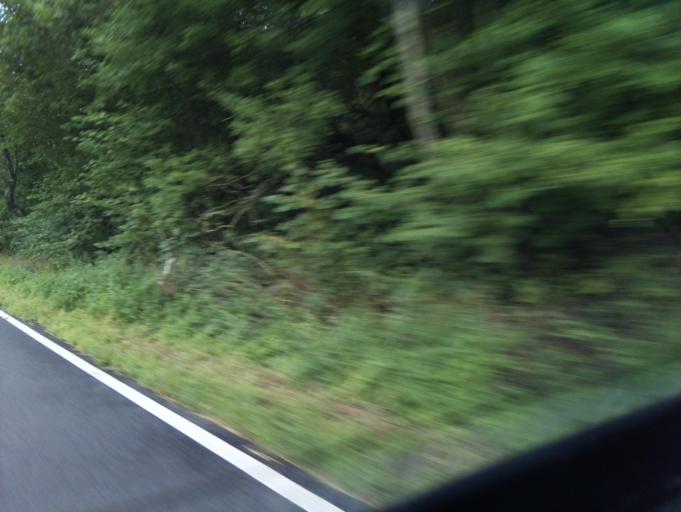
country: GB
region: England
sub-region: North Yorkshire
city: Leyburn
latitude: 54.4024
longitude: -1.8232
